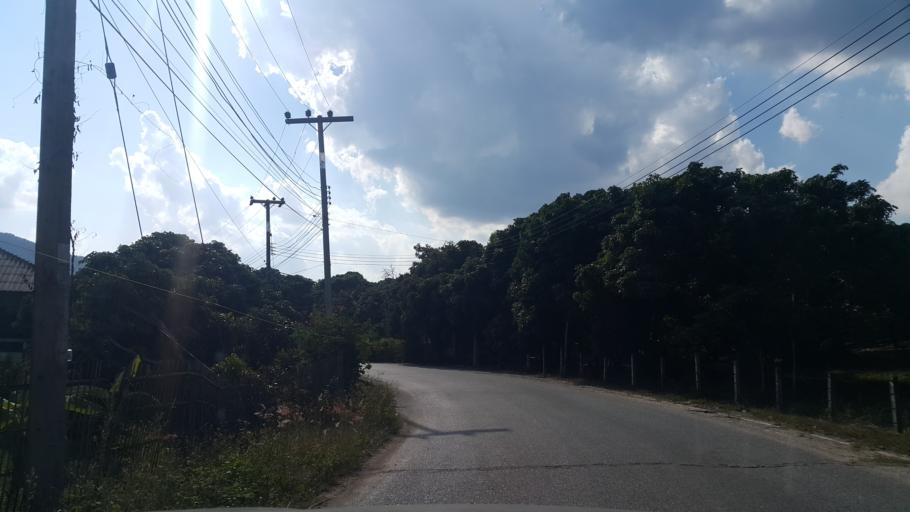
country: TH
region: Lamphun
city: Ban Thi
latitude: 18.5940
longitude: 99.1466
